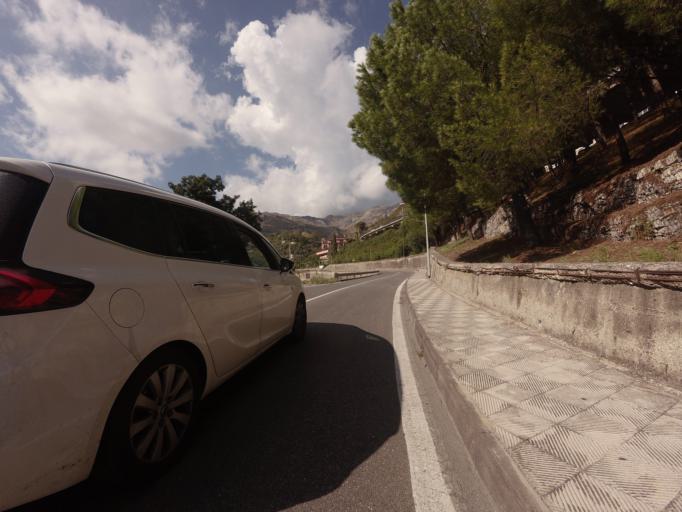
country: IT
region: Sicily
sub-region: Messina
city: Taormina
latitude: 37.8448
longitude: 15.2791
